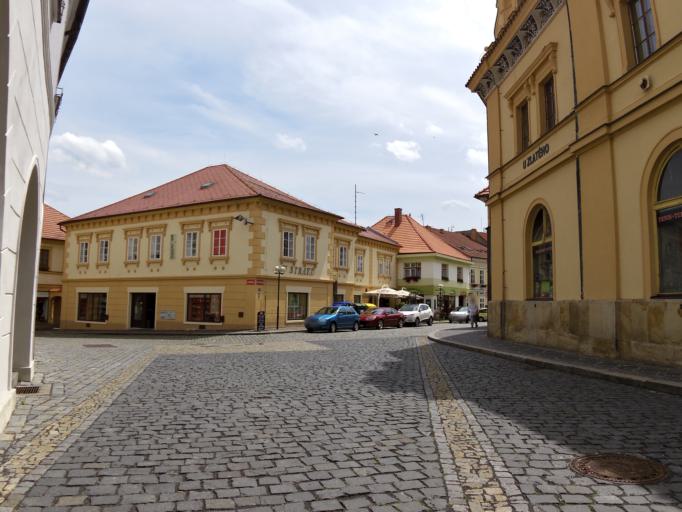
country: CZ
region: Central Bohemia
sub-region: Okres Melnik
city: Melnik
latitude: 50.3516
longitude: 14.4753
